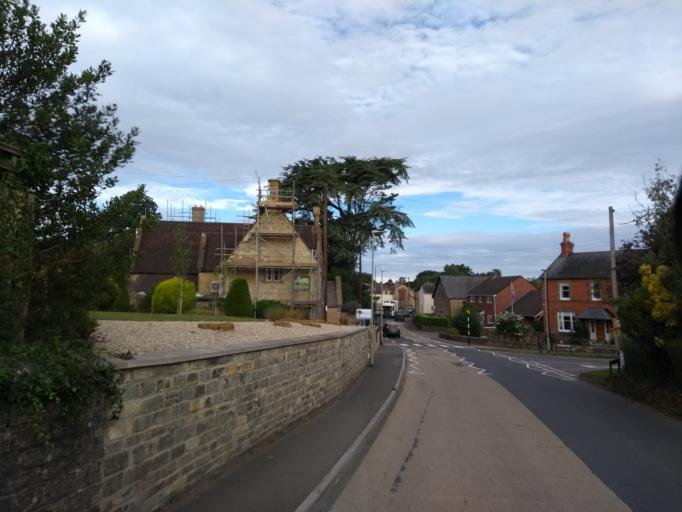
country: GB
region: England
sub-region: Somerset
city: Crewkerne
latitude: 50.8694
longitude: -2.7705
